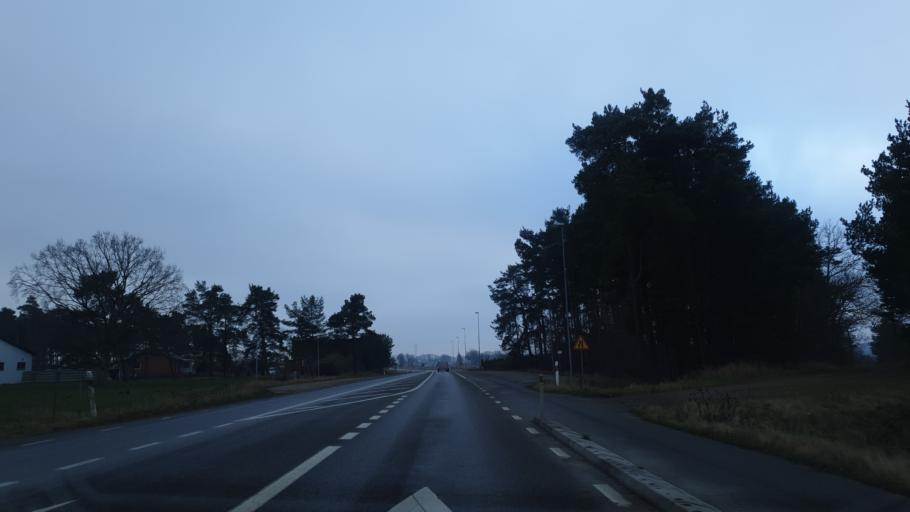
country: SE
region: Blekinge
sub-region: Solvesborgs Kommun
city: Soelvesborg
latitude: 56.0867
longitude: 14.6478
